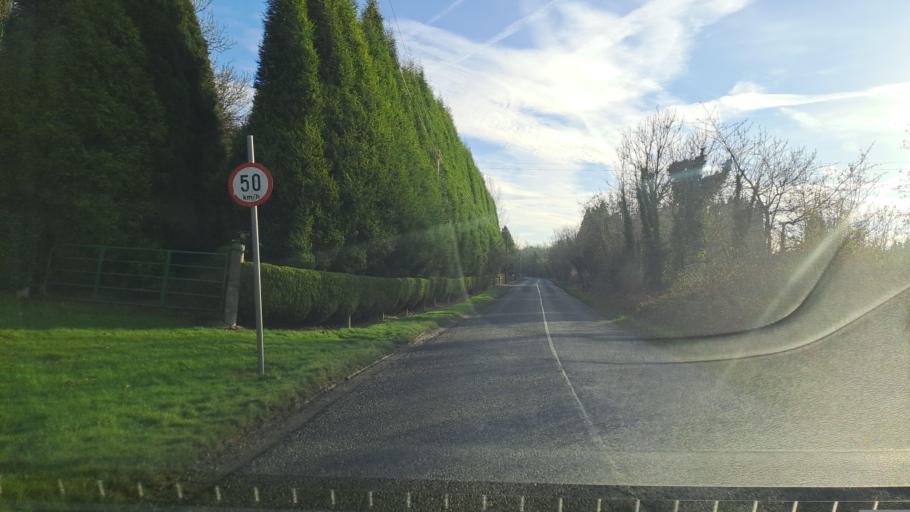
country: IE
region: Ulster
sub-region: An Cabhan
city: Kingscourt
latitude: 53.8983
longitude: -6.7689
